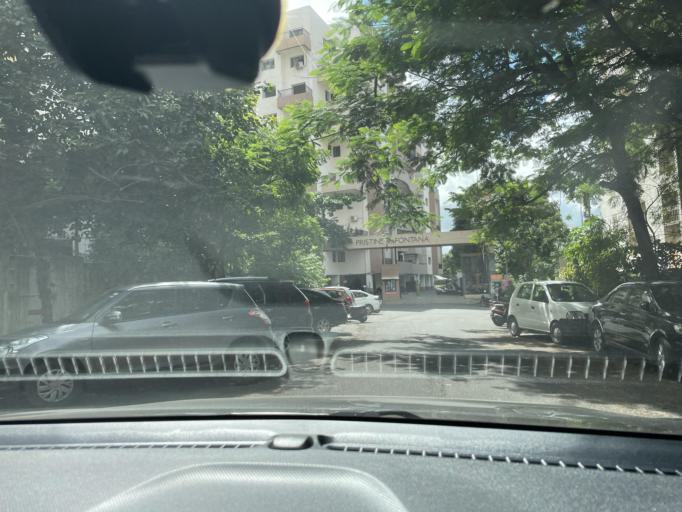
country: IN
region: Maharashtra
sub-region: Pune Division
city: Kharakvasla
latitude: 18.5095
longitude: 73.7777
